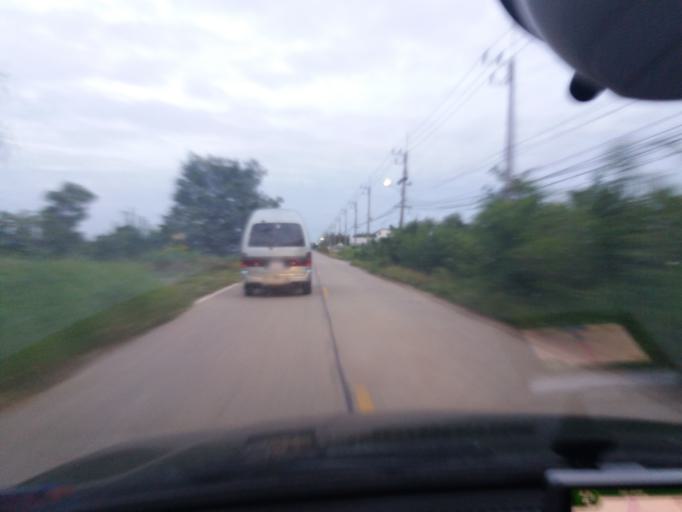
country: TH
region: Suphan Buri
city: Ban Sam Chuk
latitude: 14.7359
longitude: 100.0924
